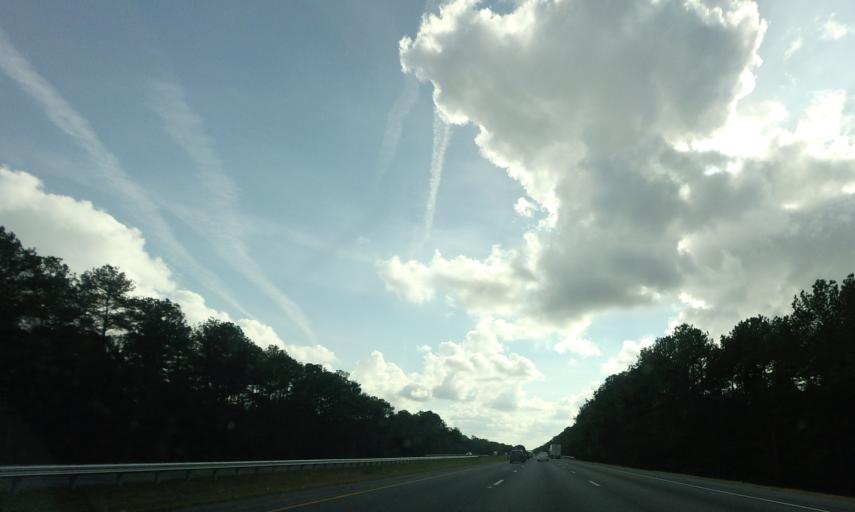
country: US
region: Georgia
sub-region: Houston County
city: Perry
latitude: 32.3803
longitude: -83.7681
